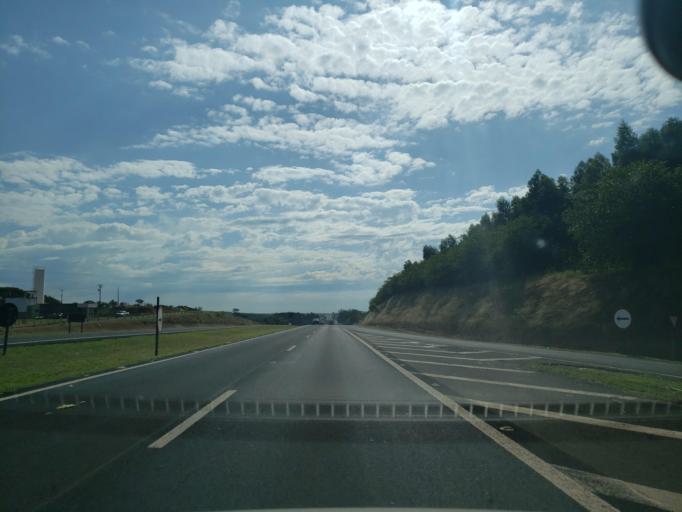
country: BR
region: Sao Paulo
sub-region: Pirajui
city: Pirajui
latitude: -21.9917
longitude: -49.4388
